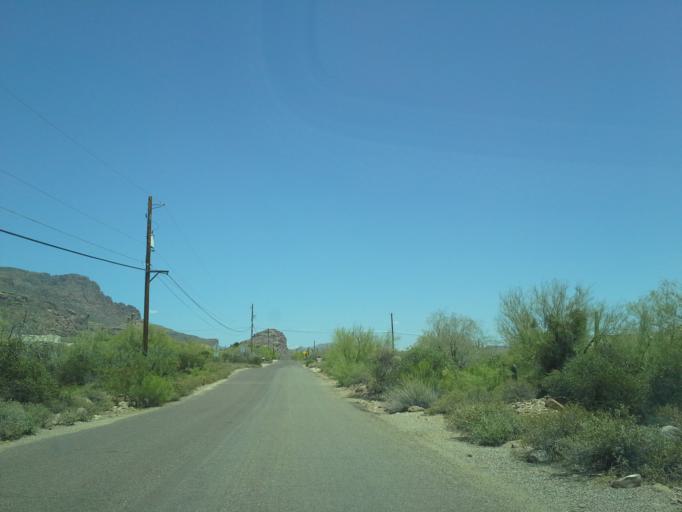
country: US
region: Arizona
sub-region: Pinal County
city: Apache Junction
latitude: 33.3898
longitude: -111.4351
